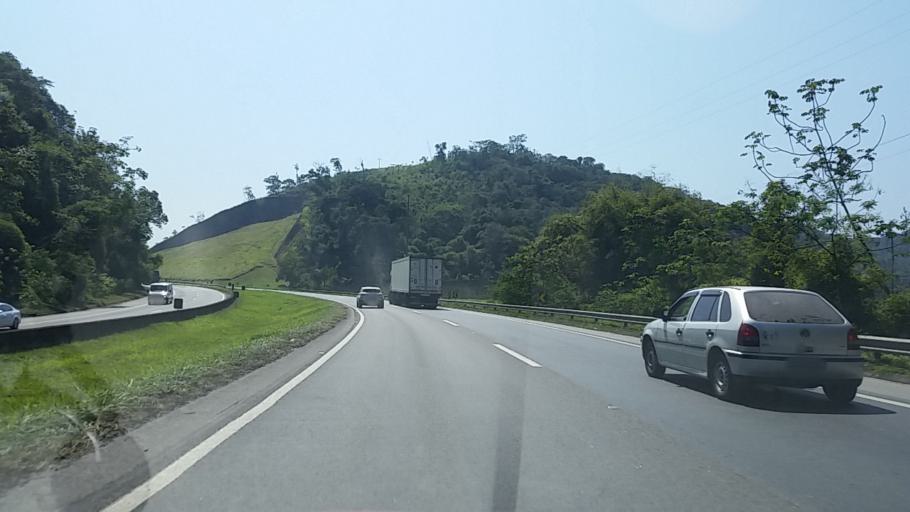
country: BR
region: Sao Paulo
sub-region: Miracatu
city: Miracatu
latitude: -24.1933
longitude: -47.3602
